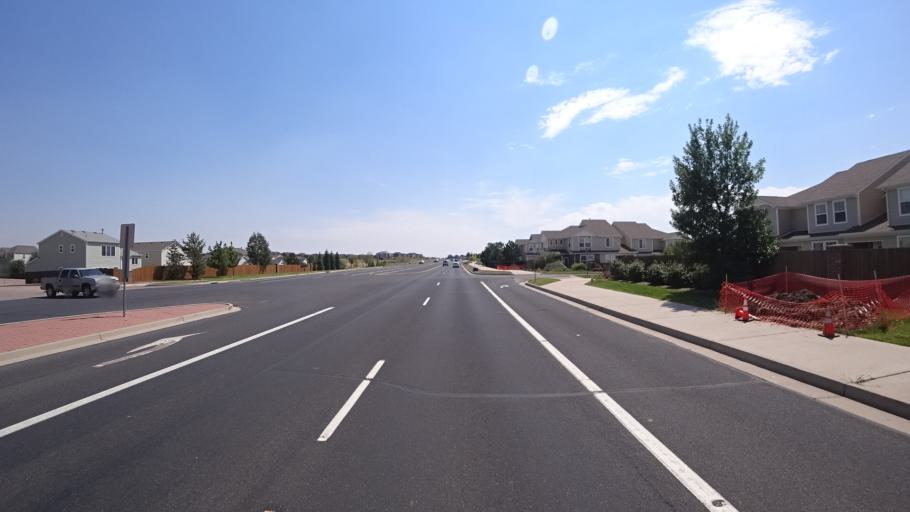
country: US
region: Colorado
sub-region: El Paso County
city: Cimarron Hills
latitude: 38.9260
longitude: -104.6973
